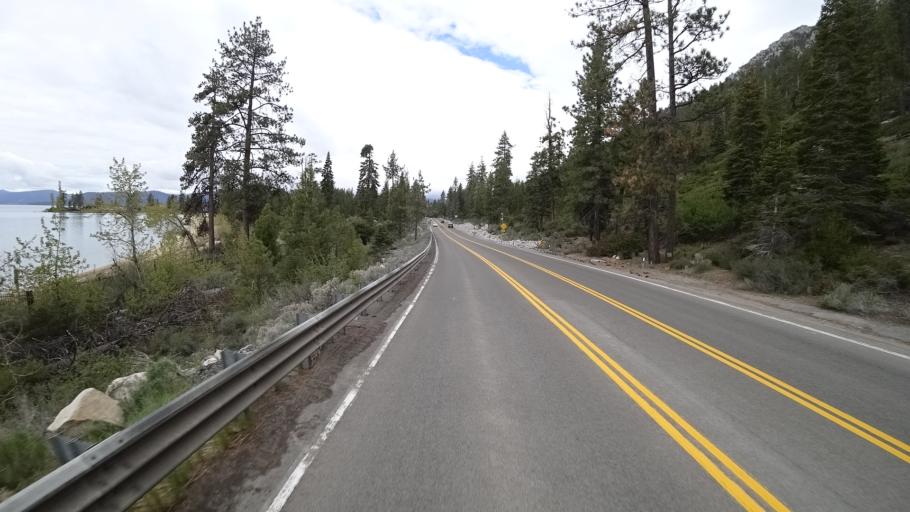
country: US
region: Nevada
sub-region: Washoe County
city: Incline Village
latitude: 39.1942
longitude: -119.9269
